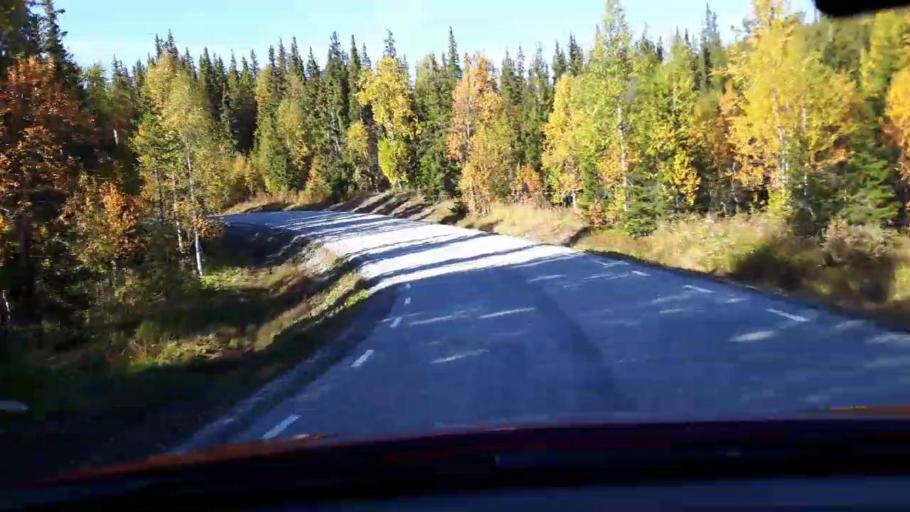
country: NO
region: Nord-Trondelag
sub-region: Royrvik
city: Royrvik
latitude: 64.8155
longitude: 14.1997
